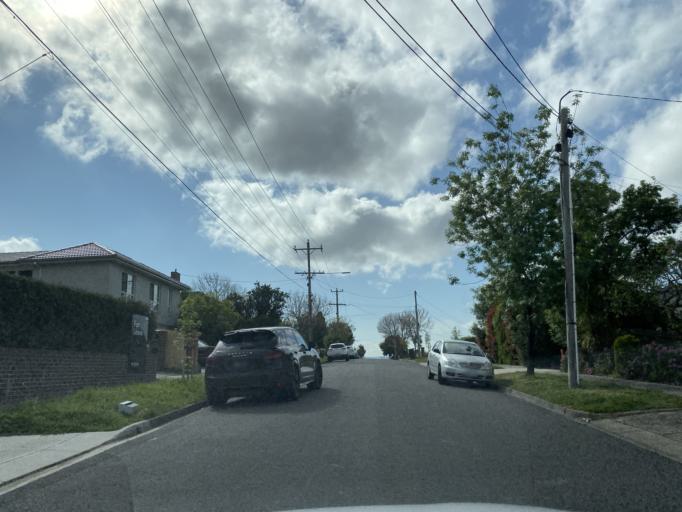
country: AU
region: Victoria
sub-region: Whitehorse
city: Burwood
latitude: -37.8409
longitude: 145.1144
